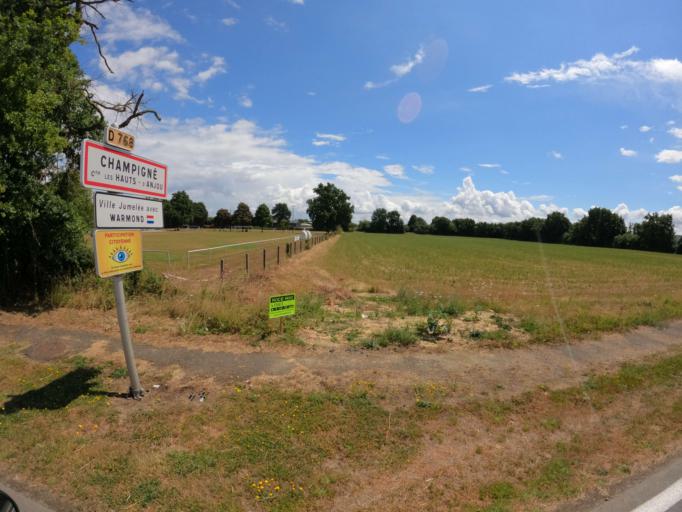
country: FR
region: Pays de la Loire
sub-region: Departement de Maine-et-Loire
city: Champigne
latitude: 47.6567
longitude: -0.5747
